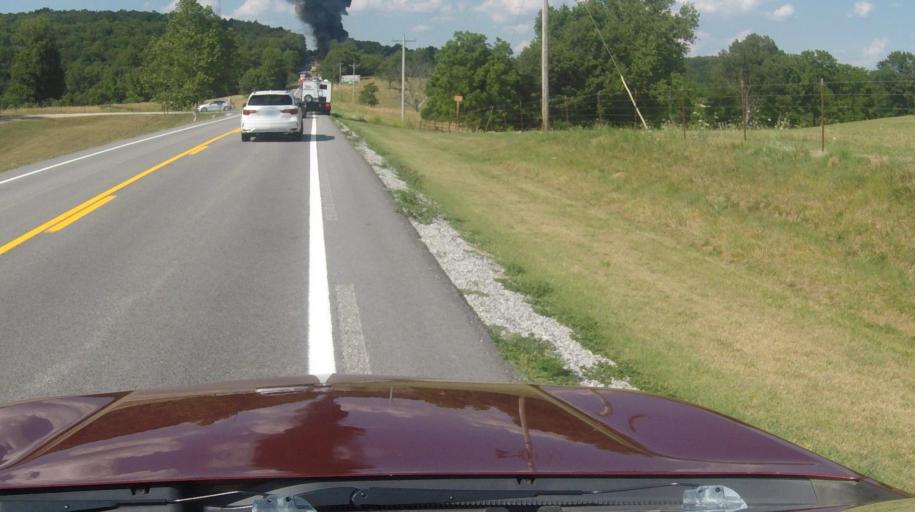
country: US
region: Arkansas
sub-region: Carroll County
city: Eureka Springs
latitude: 36.2836
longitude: -93.7659
